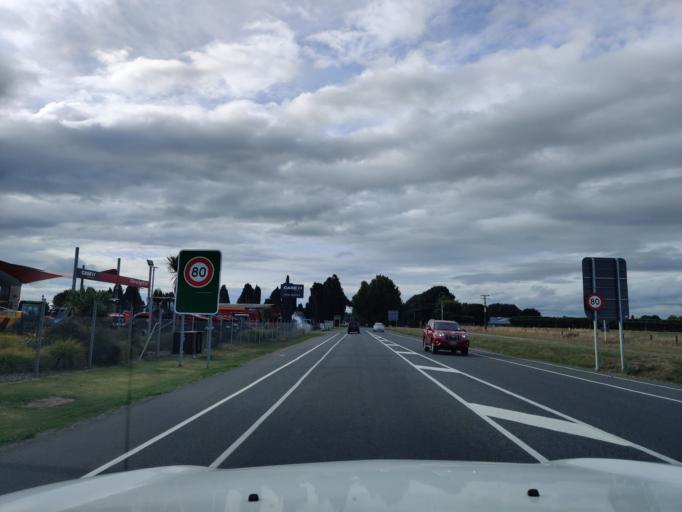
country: NZ
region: Waikato
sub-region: Waipa District
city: Cambridge
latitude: -37.8660
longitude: 175.4570
